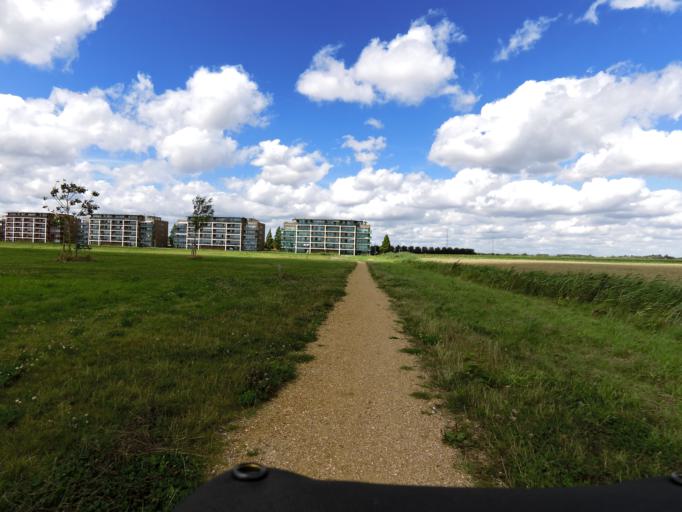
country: NL
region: South Holland
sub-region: Gemeente Oud-Beijerland
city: Oud-Beijerland
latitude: 51.8267
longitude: 4.3750
